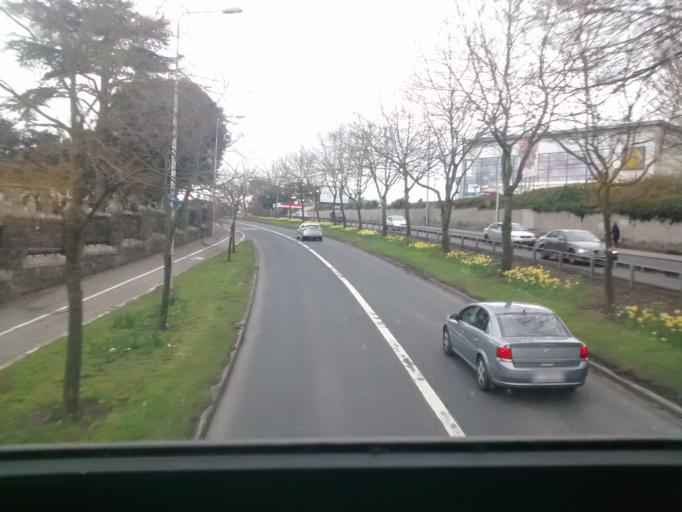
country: IE
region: Leinster
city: Cabra
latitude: 53.3745
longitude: -6.2857
